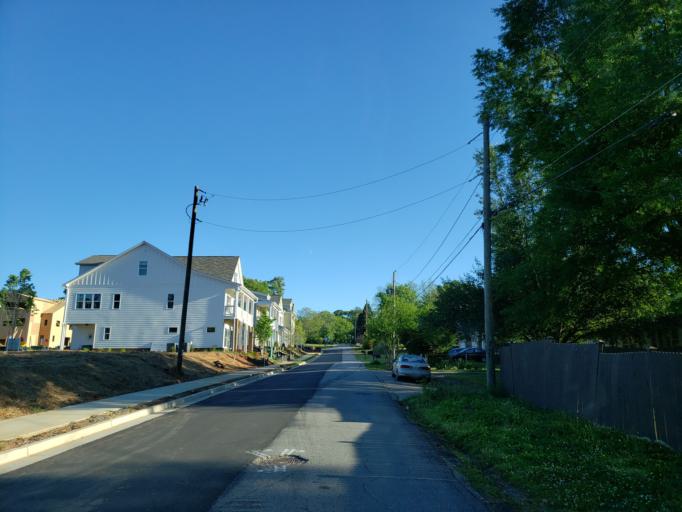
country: US
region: Georgia
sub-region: Cobb County
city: Smyrna
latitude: 33.8932
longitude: -84.5136
